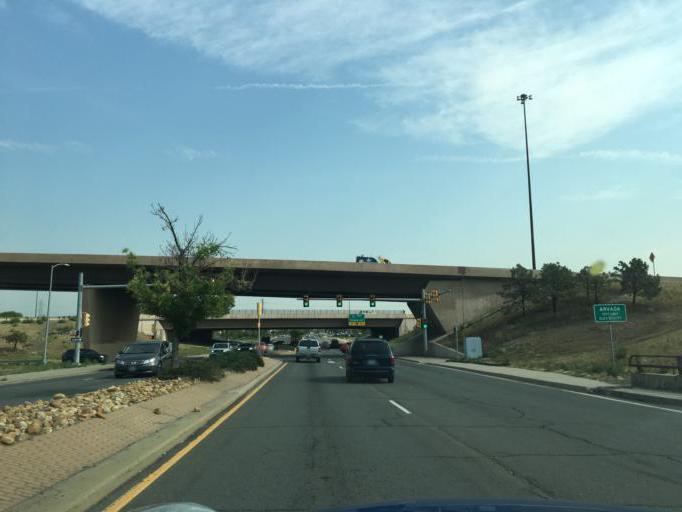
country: US
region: Colorado
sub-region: Jefferson County
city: Wheat Ridge
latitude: 39.7843
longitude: -105.0814
